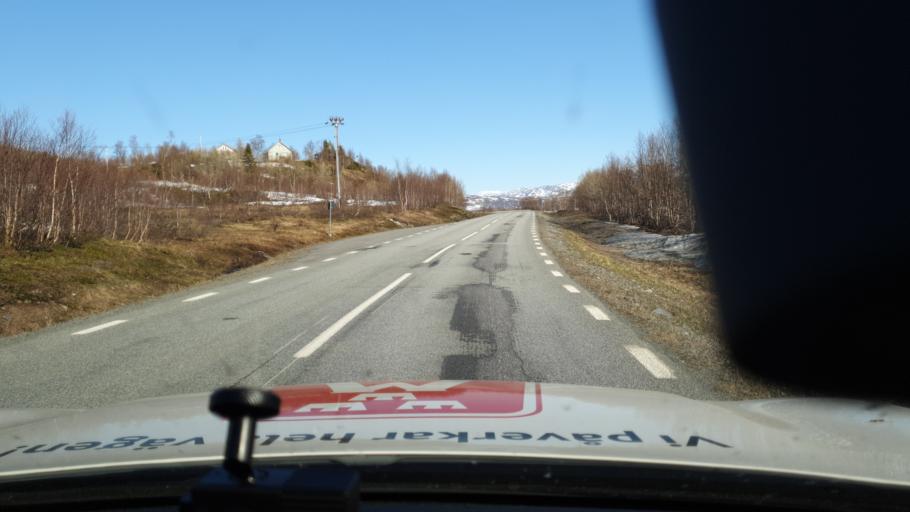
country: NO
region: Nordland
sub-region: Rana
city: Mo i Rana
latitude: 66.1260
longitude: 14.6605
